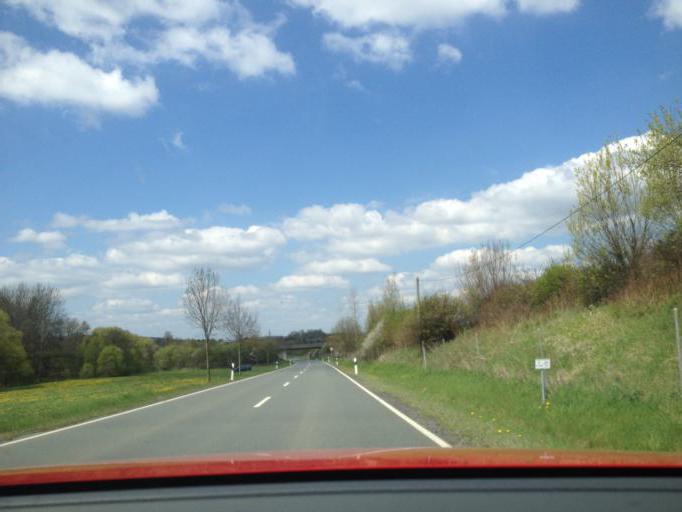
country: DE
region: Bavaria
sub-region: Upper Franconia
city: Marktredwitz
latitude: 49.9960
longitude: 12.1218
